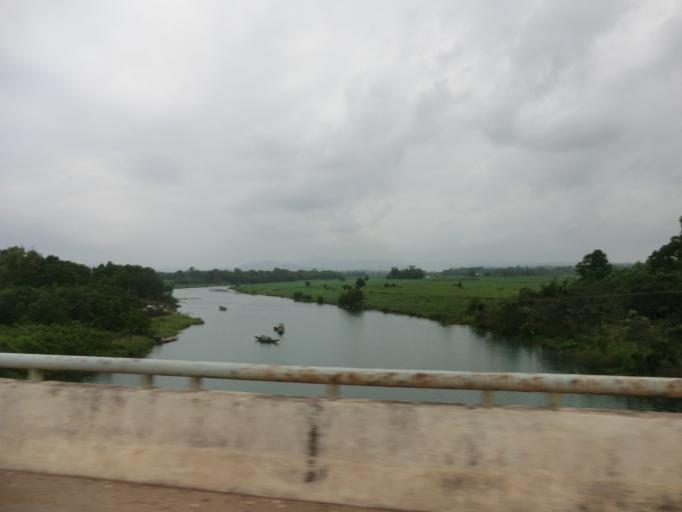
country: VN
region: Quang Tri
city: Cam Lo
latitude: 16.8199
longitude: 107.0125
